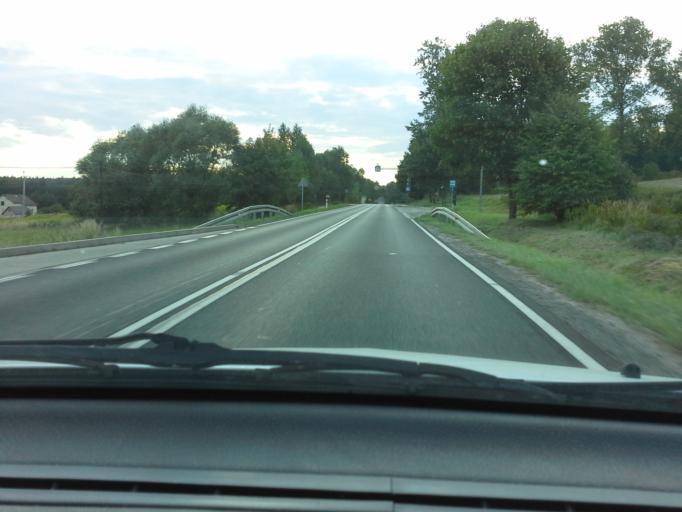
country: PL
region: Lesser Poland Voivodeship
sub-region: Powiat krakowski
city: Wola Filipowska
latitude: 50.1367
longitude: 19.5657
